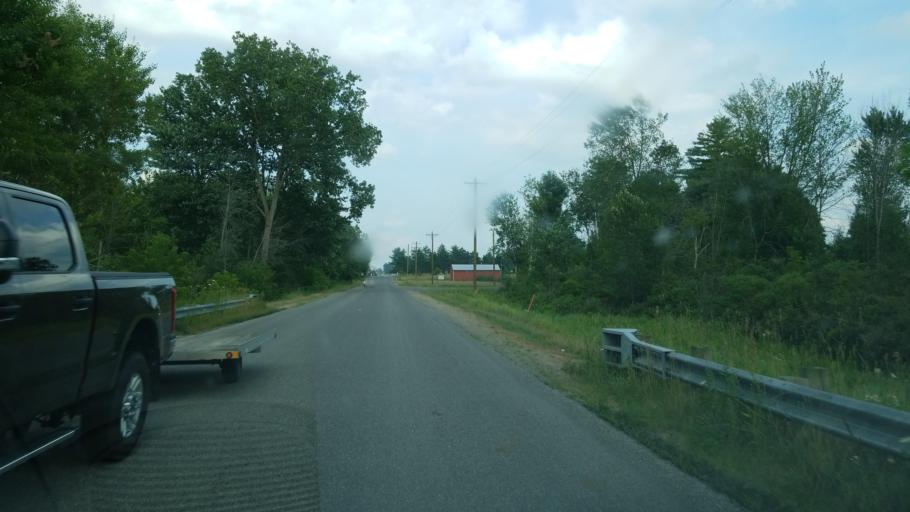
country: US
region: Michigan
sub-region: Mecosta County
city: Canadian Lakes
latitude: 43.5400
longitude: -85.3057
